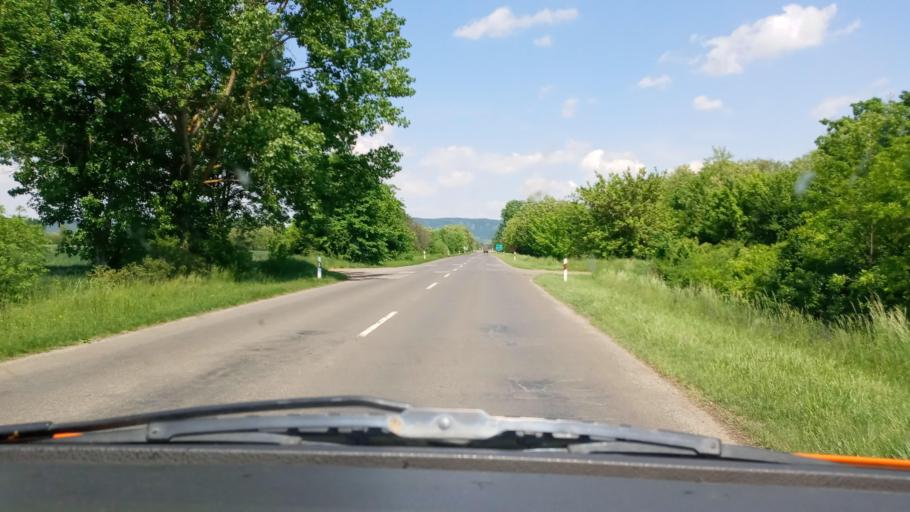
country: HU
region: Baranya
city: Harkany
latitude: 45.8320
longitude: 18.2249
